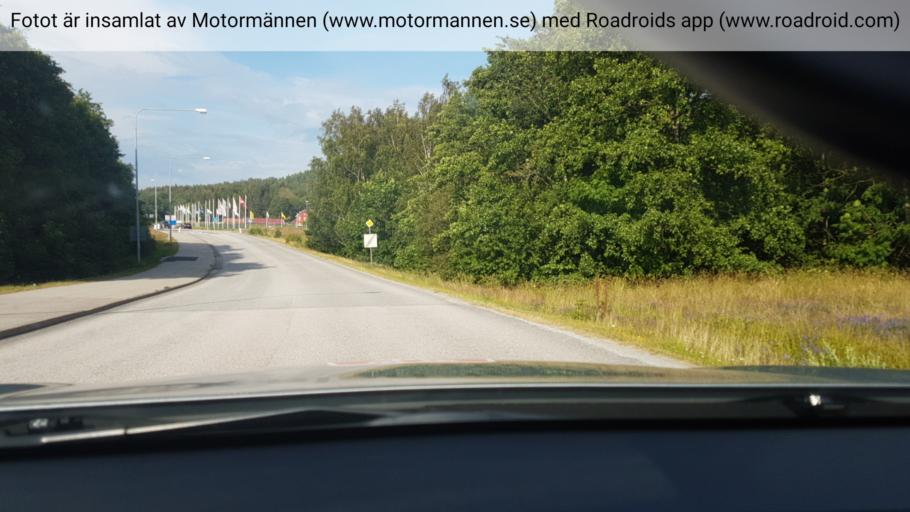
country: SE
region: Vaestra Goetaland
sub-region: Stenungsunds Kommun
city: Stenungsund
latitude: 58.0670
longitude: 11.8527
